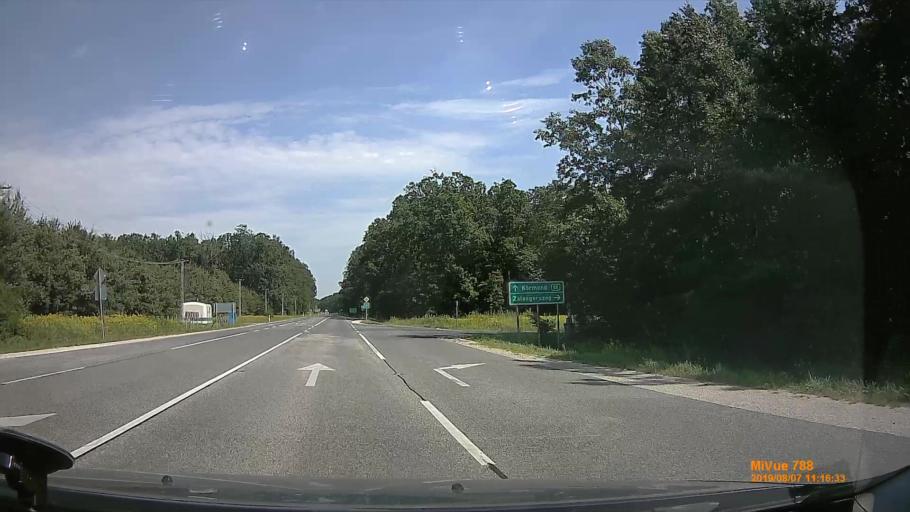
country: HU
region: Zala
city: Lenti
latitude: 46.7290
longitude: 16.5514
